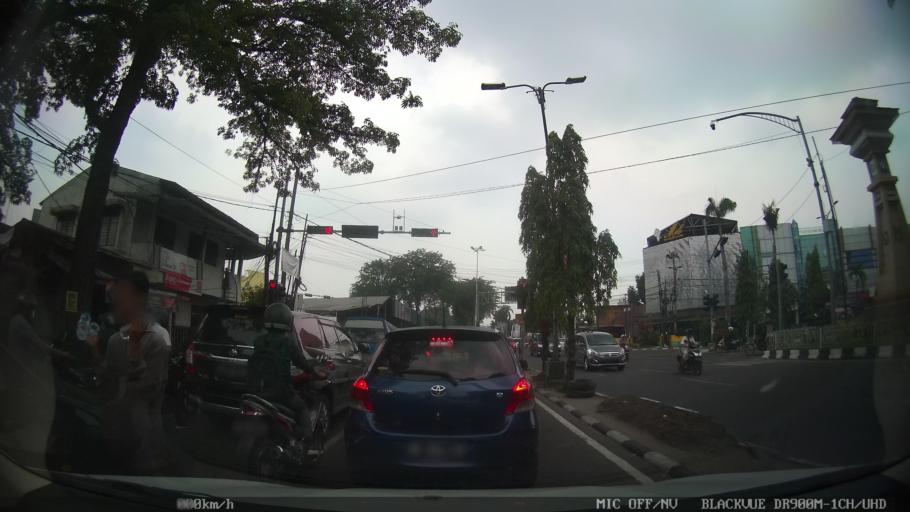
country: ID
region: North Sumatra
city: Medan
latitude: 3.5728
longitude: 98.6892
